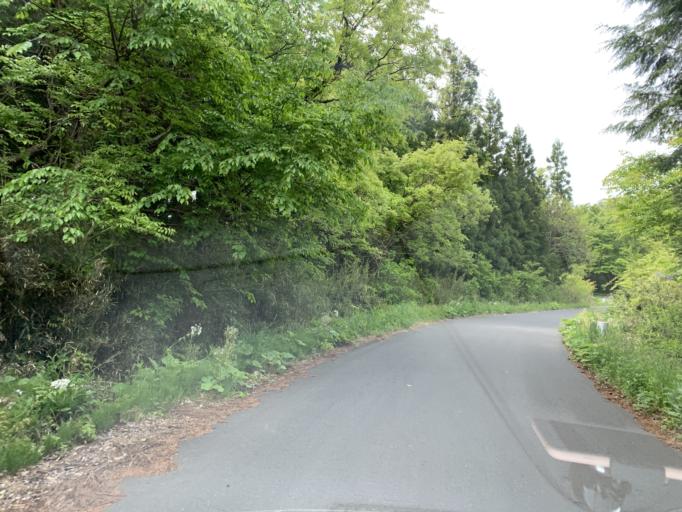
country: JP
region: Iwate
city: Ichinoseki
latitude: 38.8707
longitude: 141.0654
